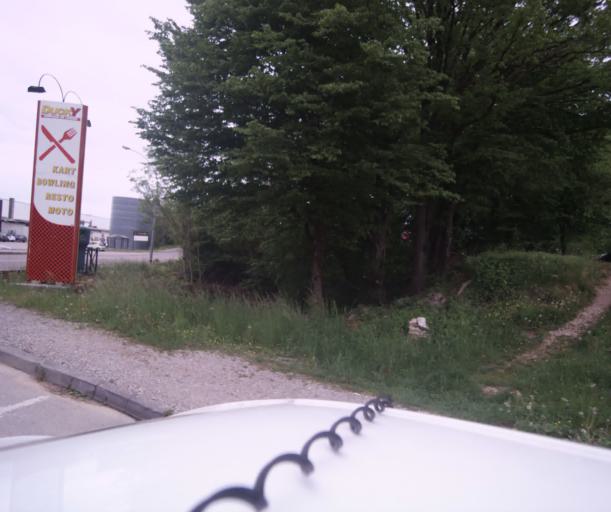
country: FR
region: Franche-Comte
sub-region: Departement du Doubs
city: Franois
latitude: 47.2136
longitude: 5.9460
